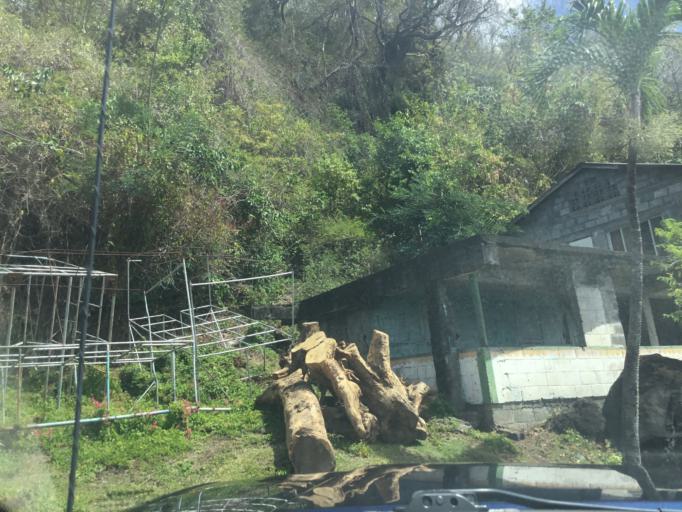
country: VC
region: Saint George
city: Kingstown Park
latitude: 13.1579
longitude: -61.2337
